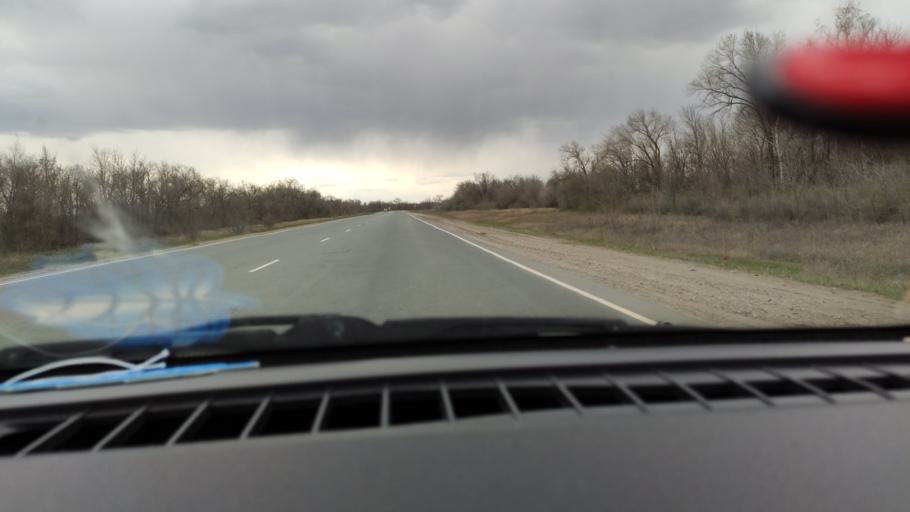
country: RU
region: Saratov
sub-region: Saratovskiy Rayon
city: Saratov
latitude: 51.7084
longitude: 46.0162
